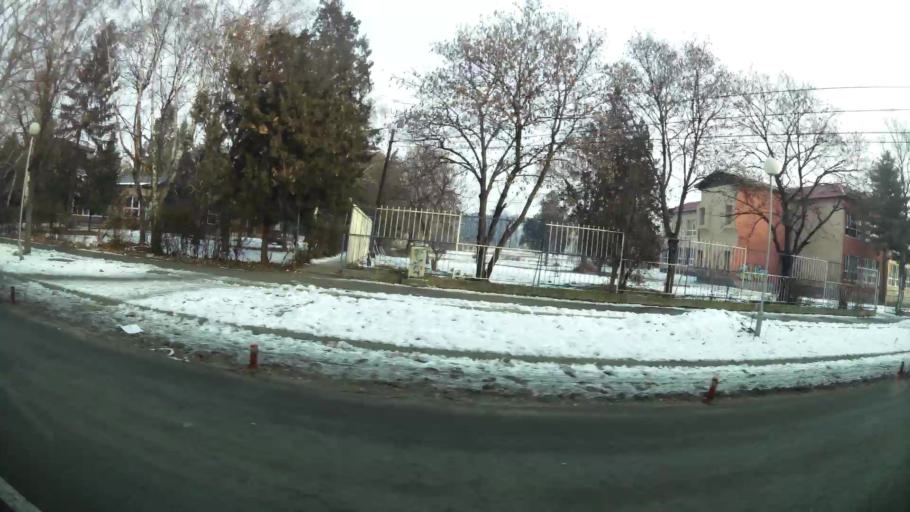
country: MK
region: Cair
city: Cair
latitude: 42.0216
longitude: 21.4418
